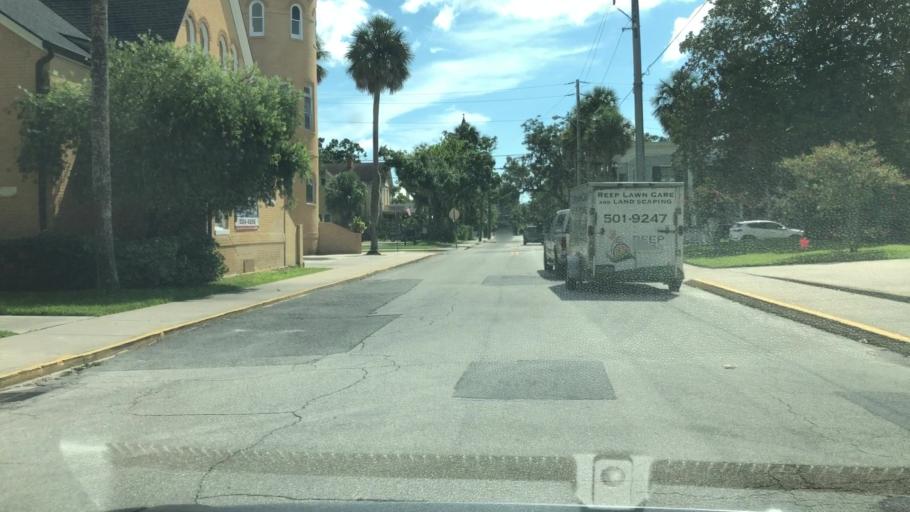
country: US
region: Florida
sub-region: Saint Johns County
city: Saint Augustine
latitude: 29.8946
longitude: -81.3172
